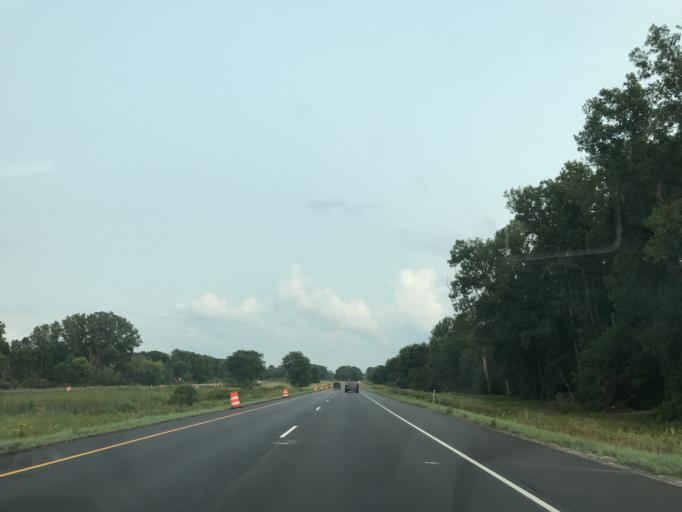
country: US
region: Michigan
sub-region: Livingston County
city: Fowlerville
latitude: 42.6410
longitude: -84.0384
